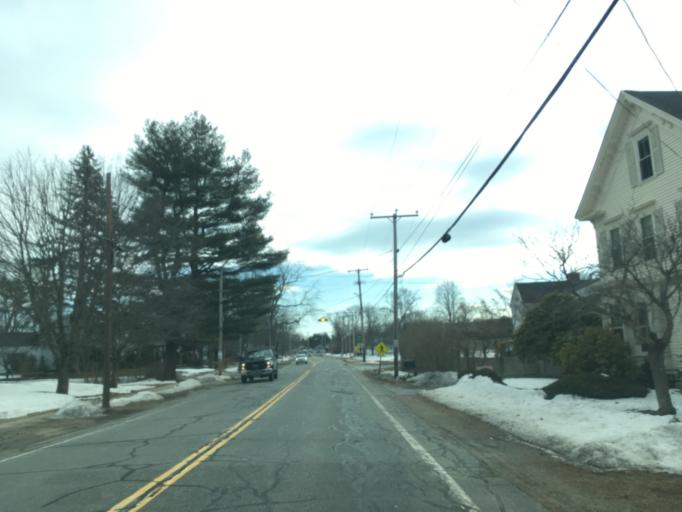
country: US
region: New Hampshire
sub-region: Rockingham County
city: Hampton
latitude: 42.9345
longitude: -70.8290
